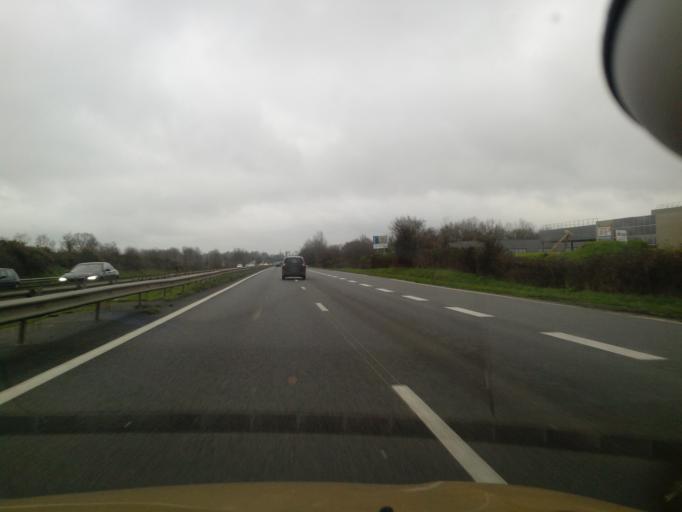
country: FR
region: Brittany
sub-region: Departement d'Ille-et-Vilaine
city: Saint-Gilles
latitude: 48.1590
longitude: -1.8311
